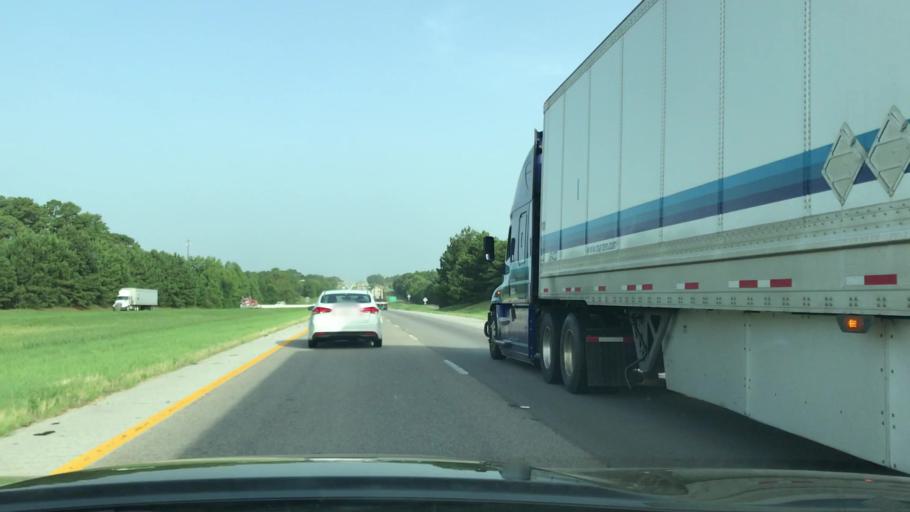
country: US
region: Texas
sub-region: Smith County
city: Hideaway
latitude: 32.4865
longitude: -95.5362
